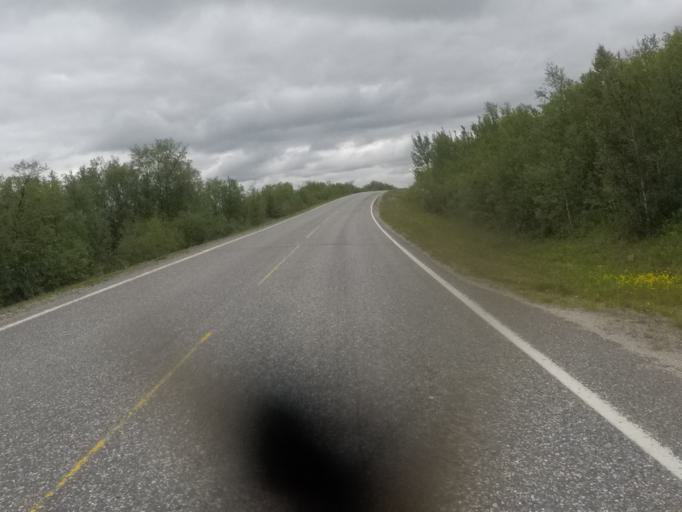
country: NO
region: Finnmark Fylke
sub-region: Kautokeino
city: Kautokeino
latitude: 68.9509
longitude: 23.0882
